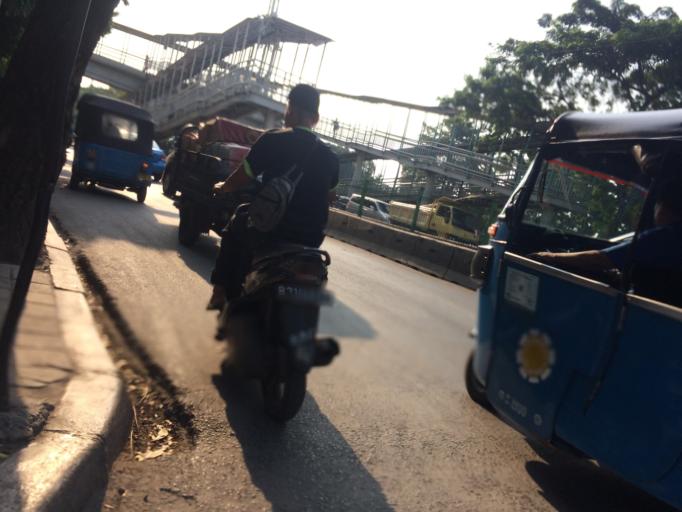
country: ID
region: Jakarta Raya
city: Jakarta
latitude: -6.2075
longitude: 106.8417
